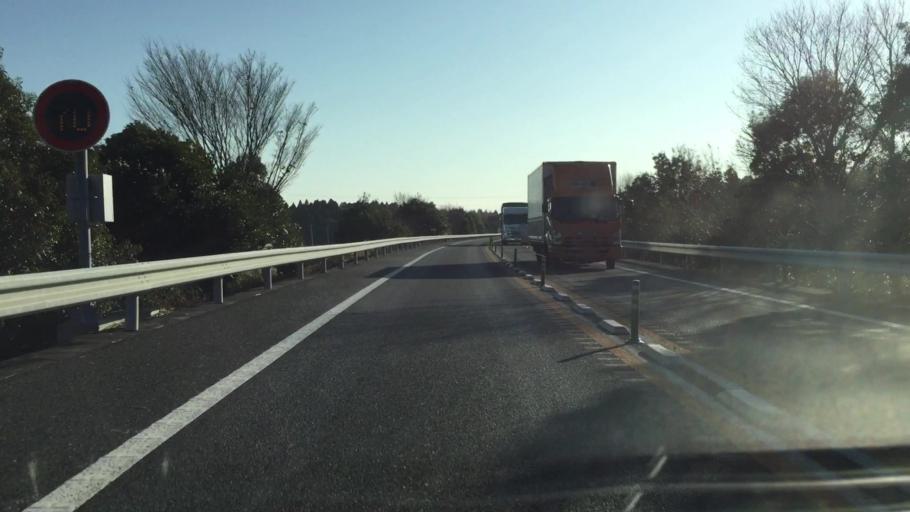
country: JP
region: Ibaraki
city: Ami
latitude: 35.9951
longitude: 140.2099
